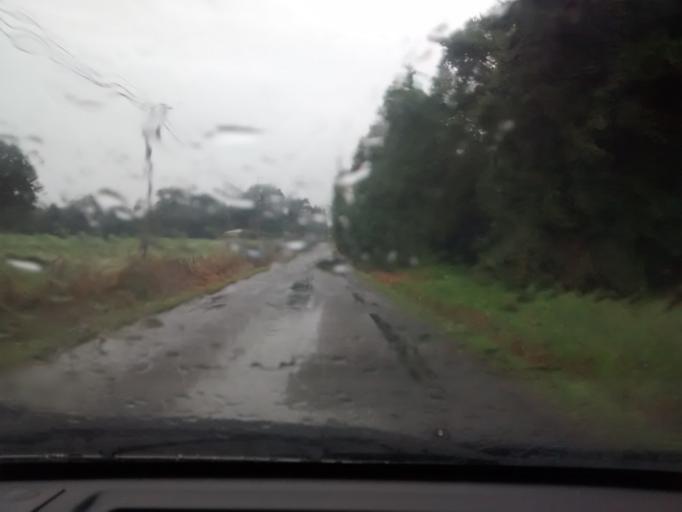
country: FR
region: Brittany
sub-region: Departement d'Ille-et-Vilaine
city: Betton
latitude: 48.1773
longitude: -1.6226
